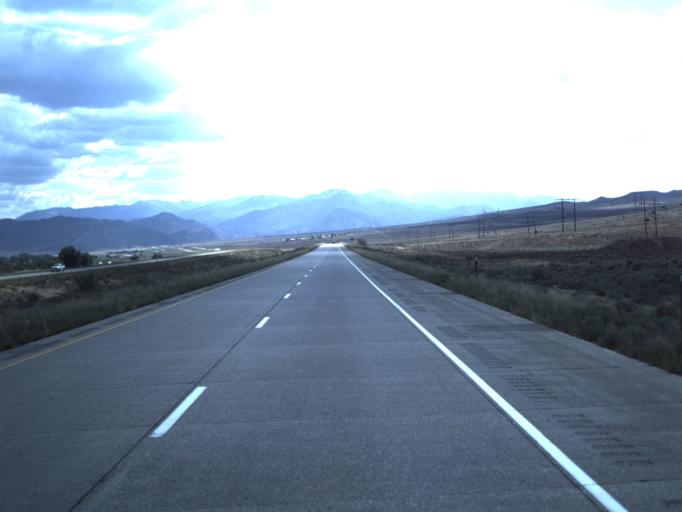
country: US
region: Utah
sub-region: Sevier County
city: Monroe
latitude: 38.6509
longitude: -112.2131
